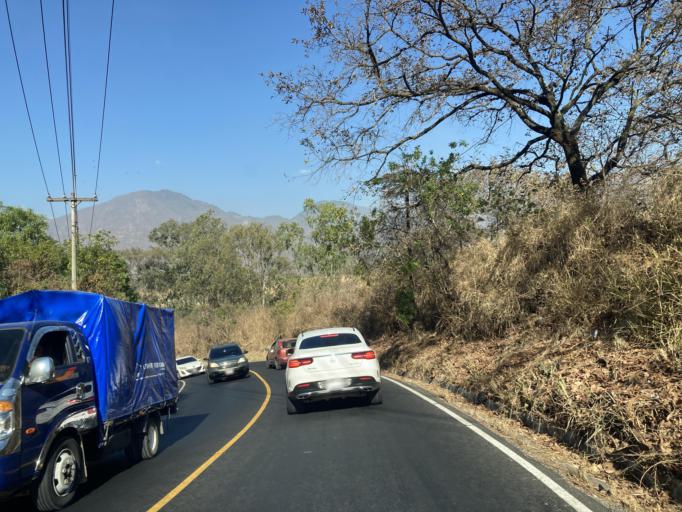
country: GT
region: Guatemala
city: Amatitlan
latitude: 14.5004
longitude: -90.6249
